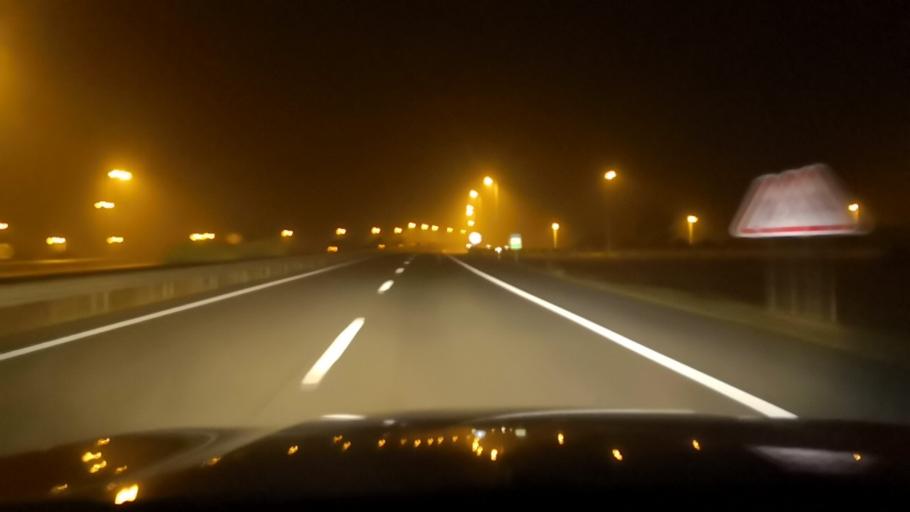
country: PT
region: Santarem
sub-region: Benavente
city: Poceirao
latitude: 38.8385
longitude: -8.7286
